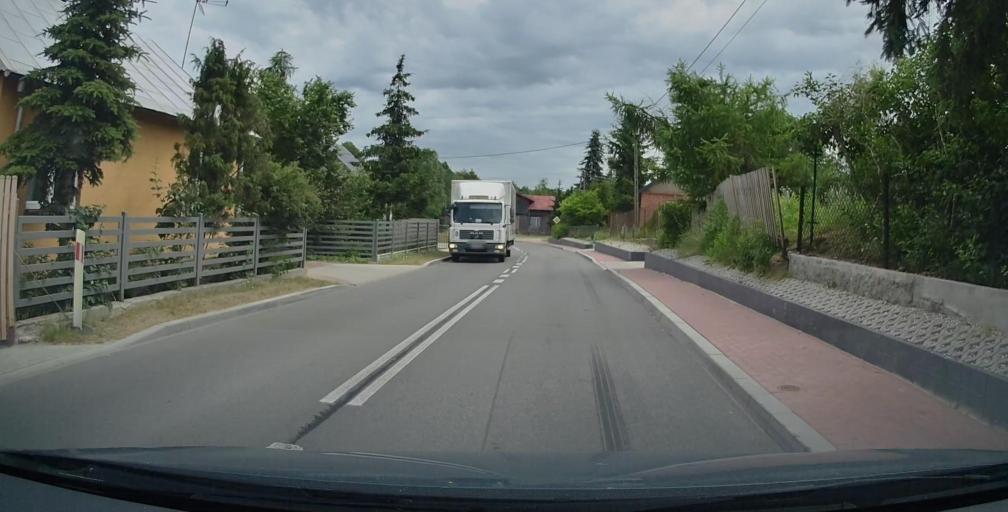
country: PL
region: Masovian Voivodeship
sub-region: Powiat losicki
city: Sarnaki
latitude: 52.3114
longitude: 22.9000
